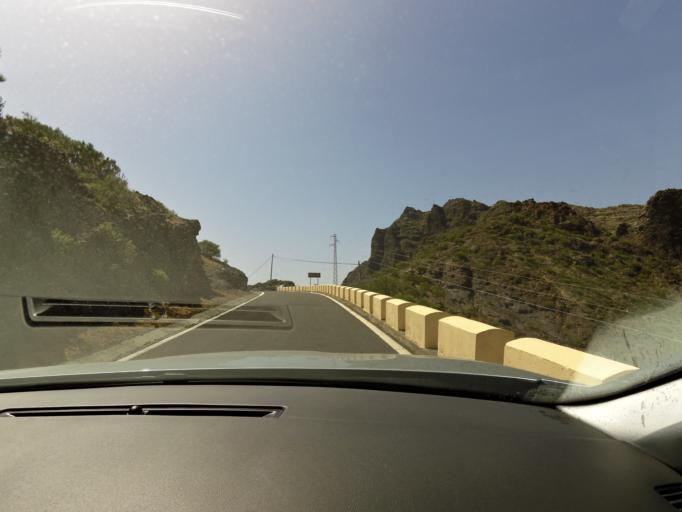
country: ES
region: Canary Islands
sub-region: Provincia de Santa Cruz de Tenerife
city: Santiago del Teide
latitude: 28.2994
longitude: -16.8235
